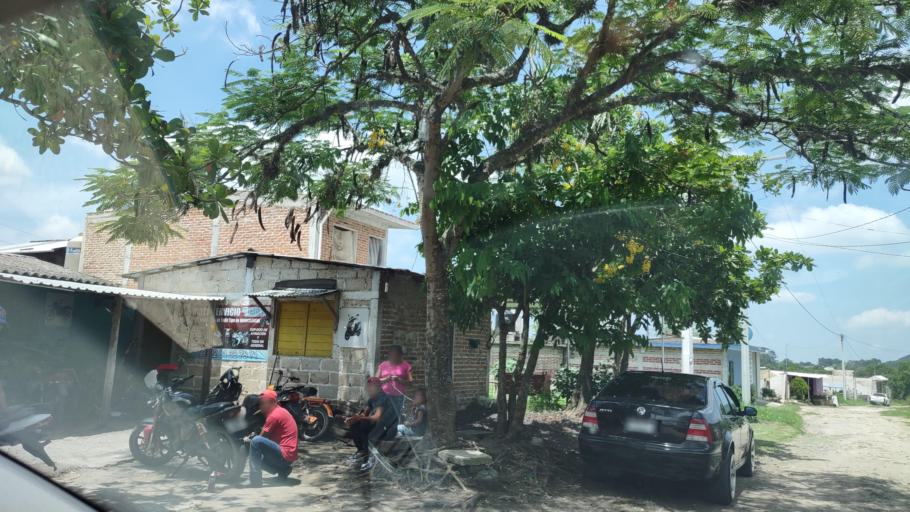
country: MX
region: Veracruz
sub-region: Emiliano Zapata
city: Dos Rios
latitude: 19.4274
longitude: -96.8056
